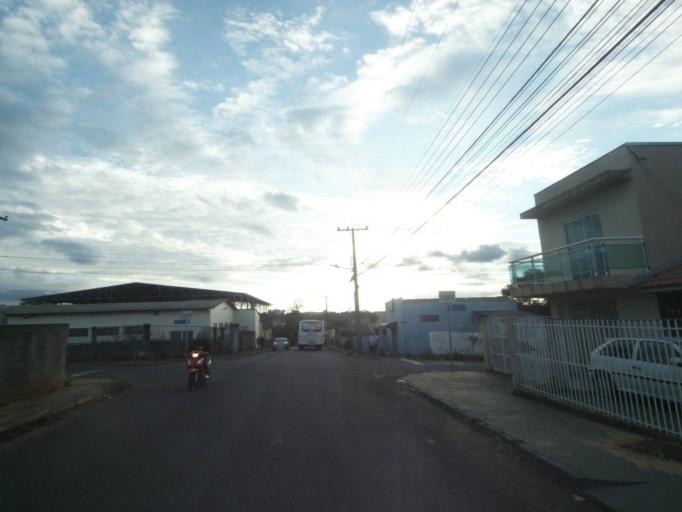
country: BR
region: Parana
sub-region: Telemaco Borba
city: Telemaco Borba
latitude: -24.3239
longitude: -50.6412
